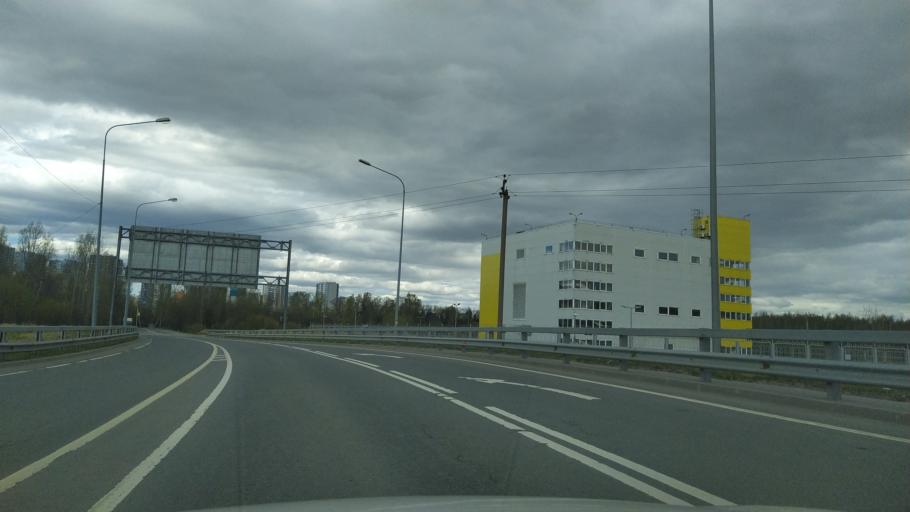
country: RU
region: Leningrad
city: Murino
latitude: 60.0219
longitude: 30.4641
